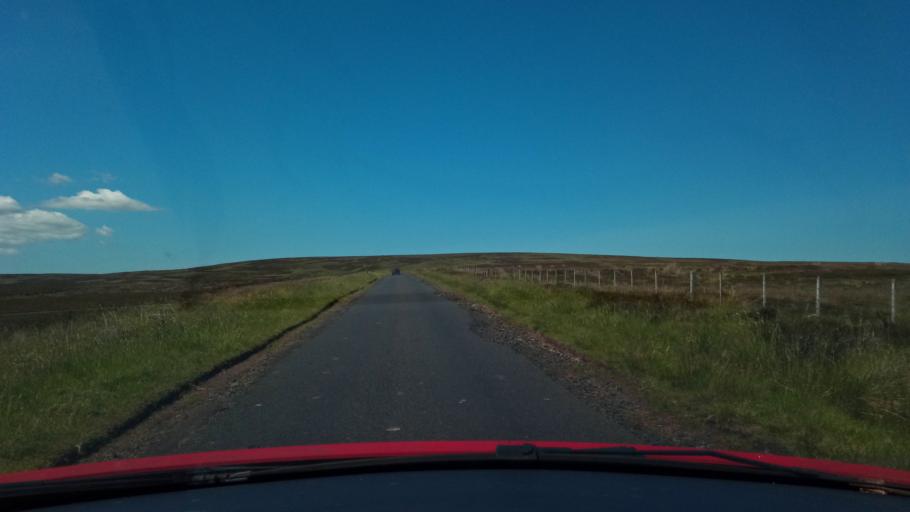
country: GB
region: Scotland
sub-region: East Lothian
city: Dunbar
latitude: 55.8287
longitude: -2.5242
